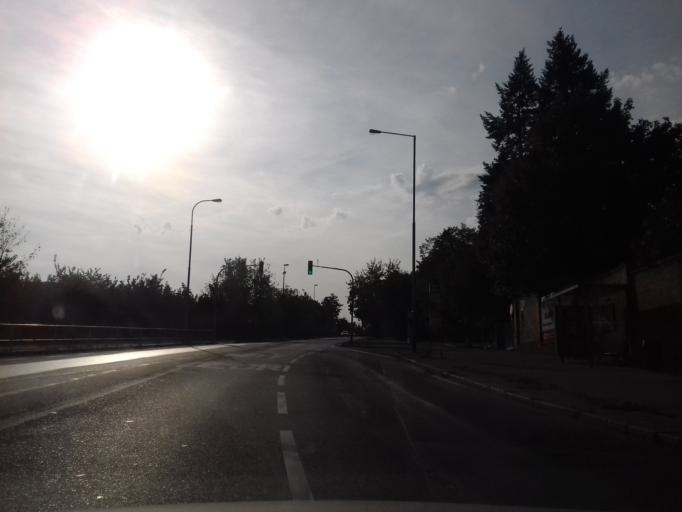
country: CZ
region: Praha
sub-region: Praha 4
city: Hodkovicky
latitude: 50.0278
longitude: 14.4572
